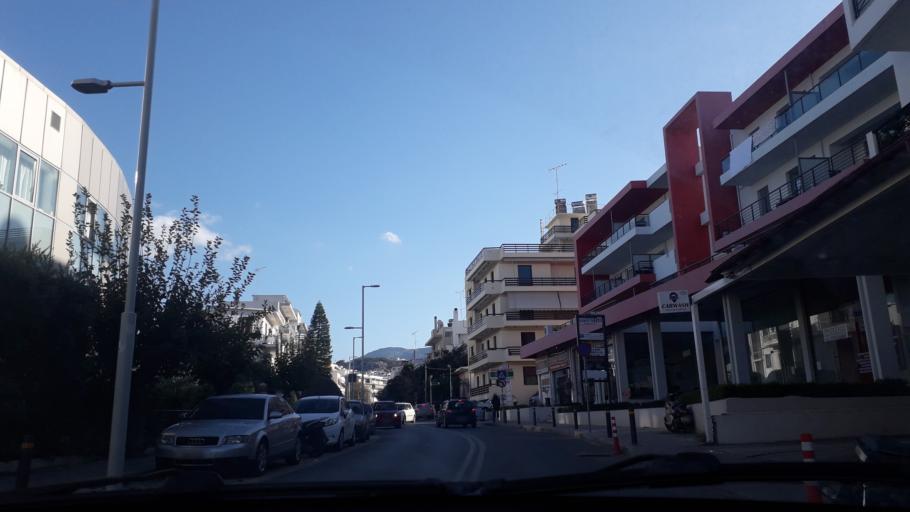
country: GR
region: Crete
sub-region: Nomos Rethymnis
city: Rethymno
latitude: 35.3652
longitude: 24.4706
